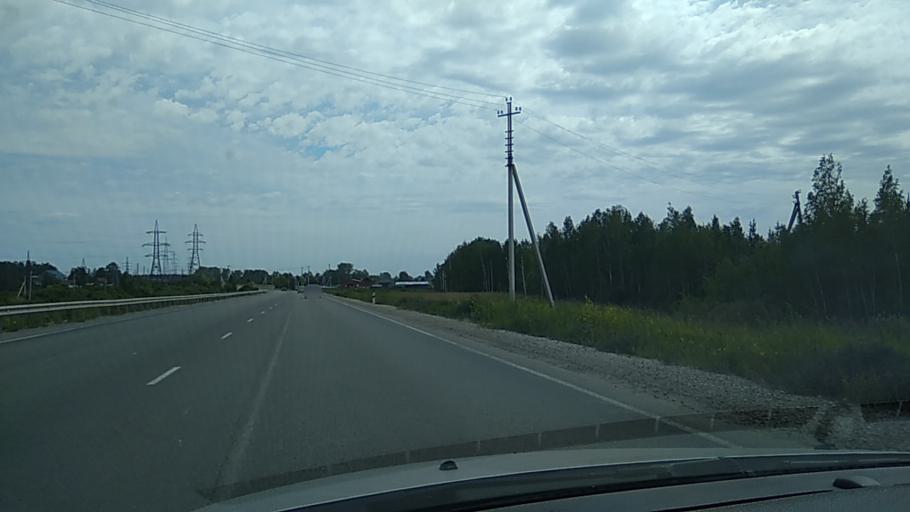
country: RU
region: Sverdlovsk
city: Verkhnyaya Pyshma
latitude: 56.9495
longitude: 60.5935
